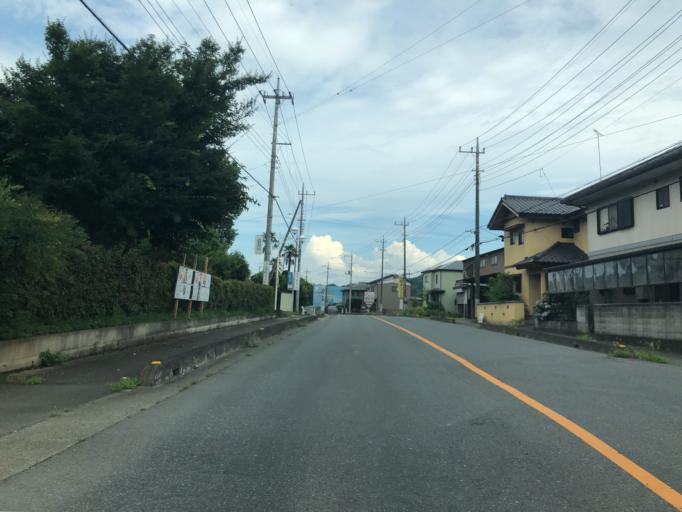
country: JP
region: Saitama
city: Fukiage-fujimi
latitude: 36.0607
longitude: 139.4094
